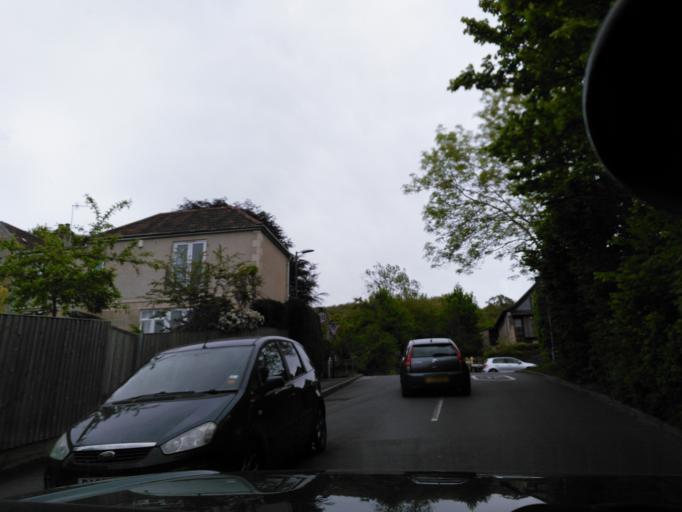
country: GB
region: England
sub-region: Bath and North East Somerset
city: Bath
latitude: 51.3923
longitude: -2.3244
